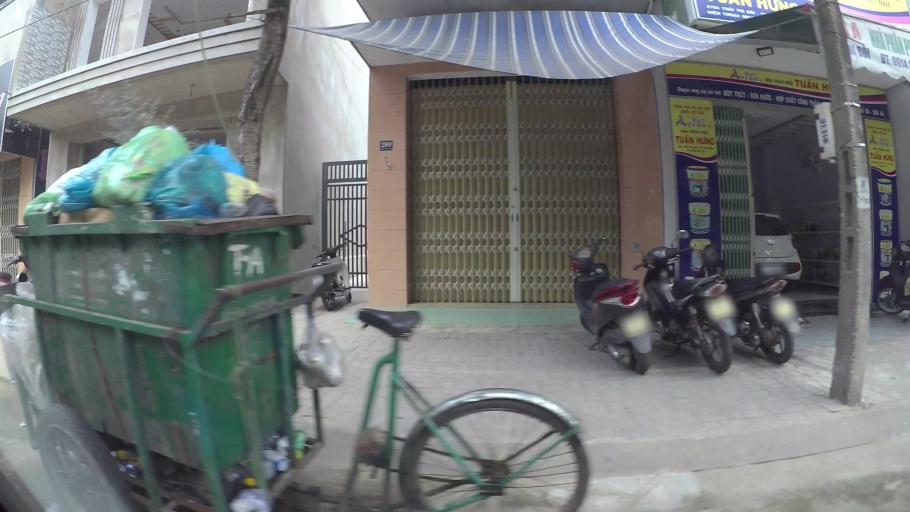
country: VN
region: Da Nang
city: Thanh Khe
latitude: 16.0684
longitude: 108.1938
